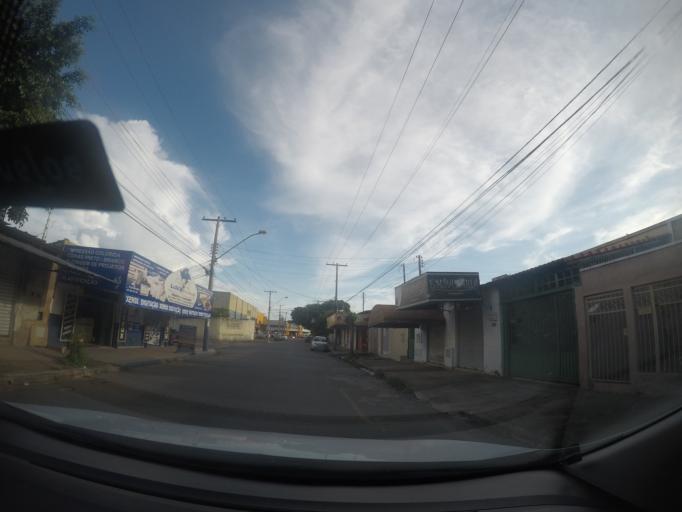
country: BR
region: Goias
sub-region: Goiania
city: Goiania
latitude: -16.6714
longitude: -49.3017
